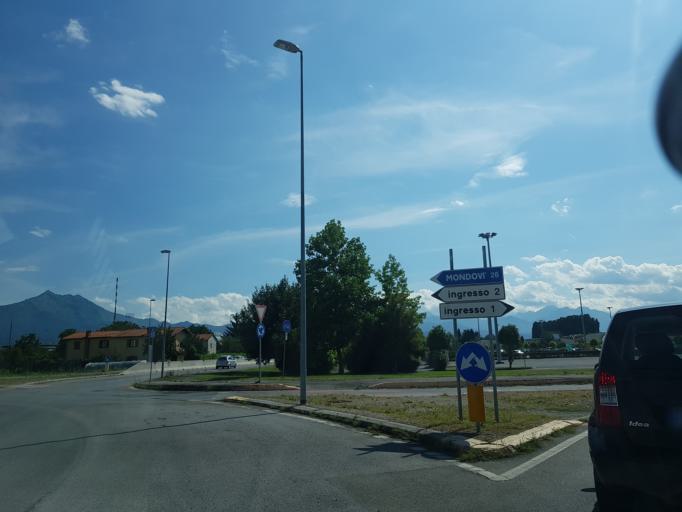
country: IT
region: Piedmont
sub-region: Provincia di Cuneo
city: Cuneo
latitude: 44.3933
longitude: 7.5859
